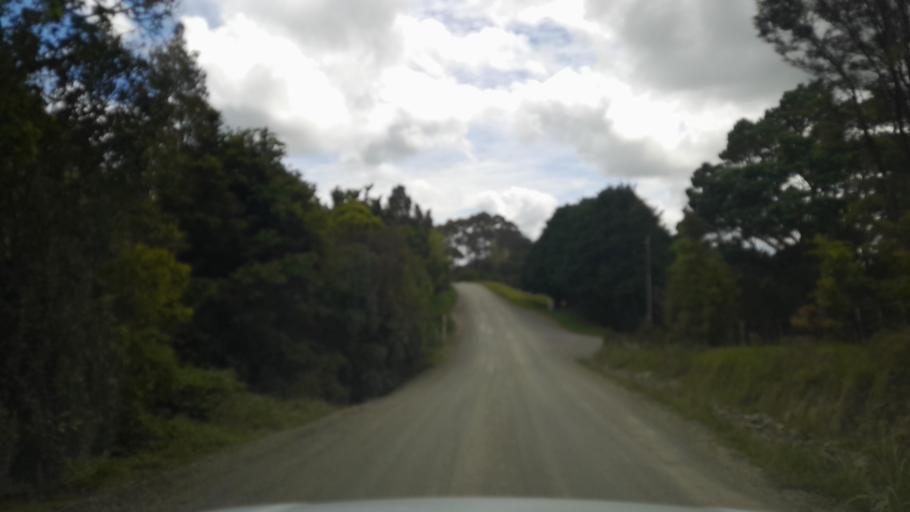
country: NZ
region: Auckland
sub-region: Auckland
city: Wellsford
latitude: -36.1660
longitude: 174.3552
